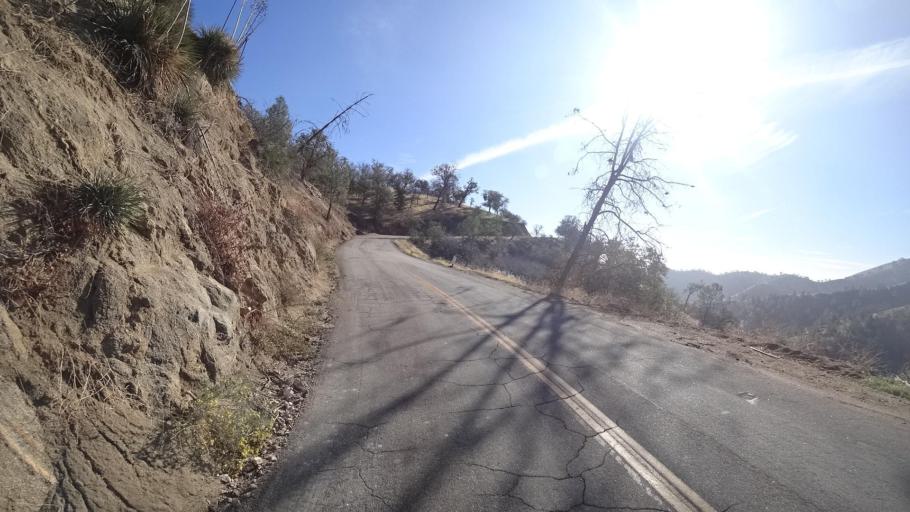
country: US
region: California
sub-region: Kern County
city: Bear Valley Springs
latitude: 35.3328
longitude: -118.5880
